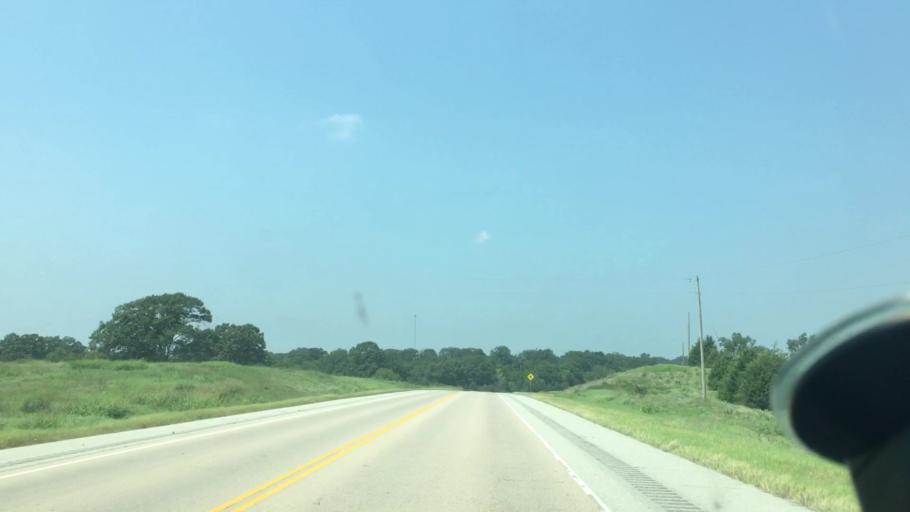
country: US
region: Oklahoma
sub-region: Atoka County
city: Atoka
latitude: 34.2891
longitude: -95.9670
